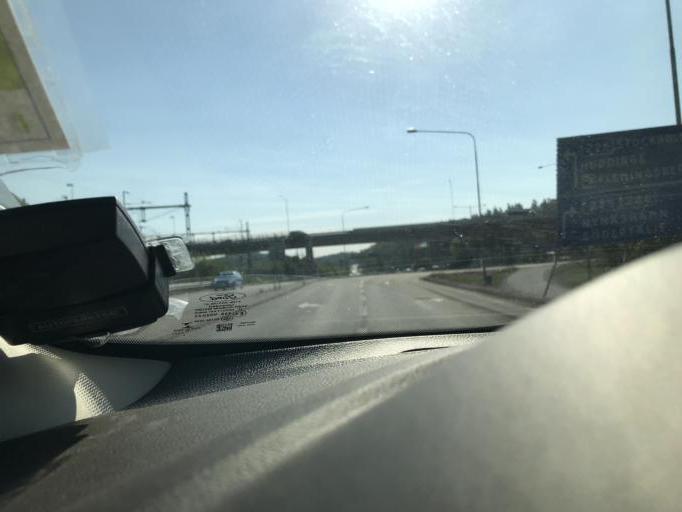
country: SE
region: Stockholm
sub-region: Botkyrka Kommun
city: Tumba
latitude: 59.1993
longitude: 17.8390
